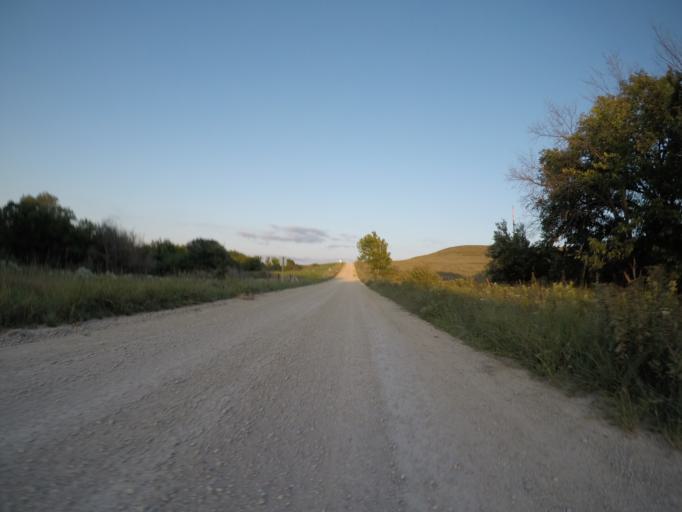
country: US
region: Kansas
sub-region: Riley County
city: Ogden
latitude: 39.0064
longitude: -96.6112
